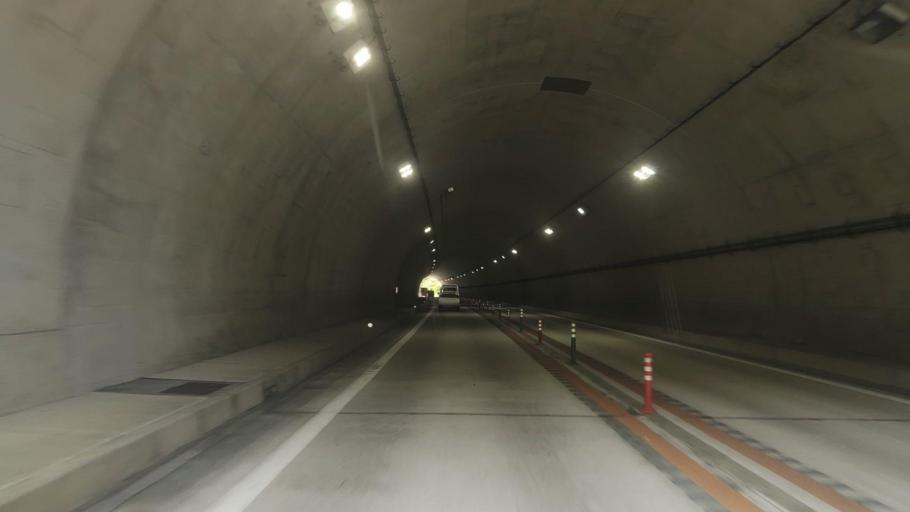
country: JP
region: Wakayama
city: Tanabe
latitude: 33.5840
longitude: 135.4501
